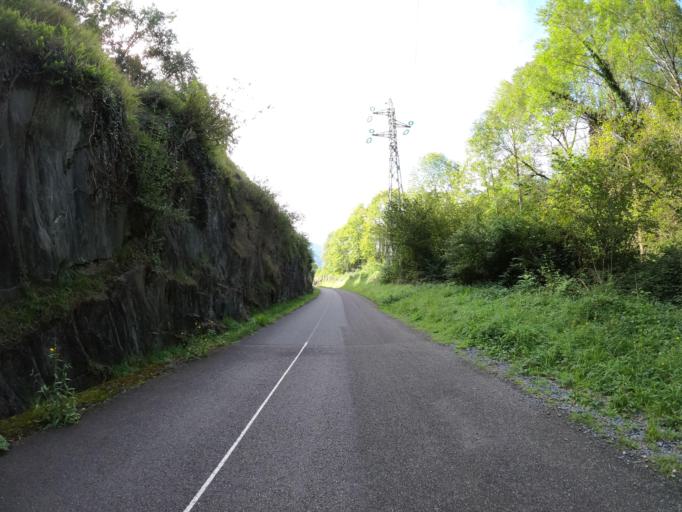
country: FR
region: Midi-Pyrenees
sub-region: Departement des Hautes-Pyrenees
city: Lourdes
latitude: 43.0700
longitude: -0.0408
